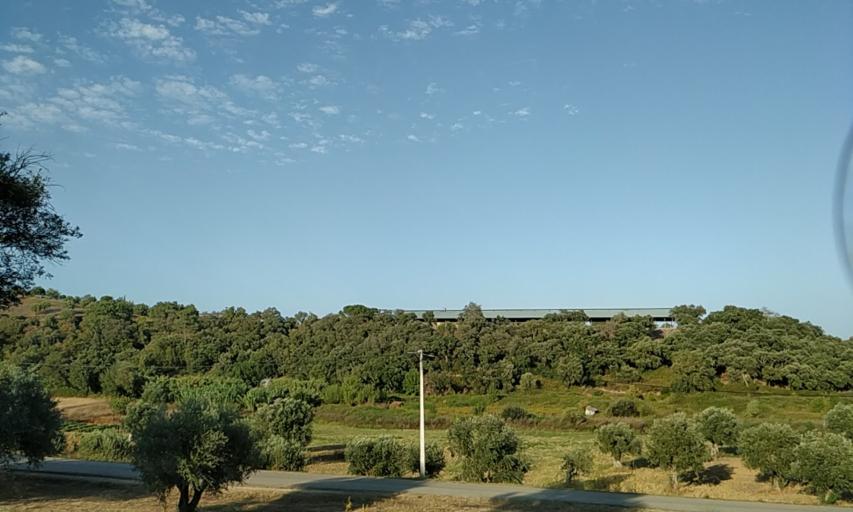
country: PT
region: Santarem
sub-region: Alcanena
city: Alcanena
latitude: 39.3590
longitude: -8.6510
